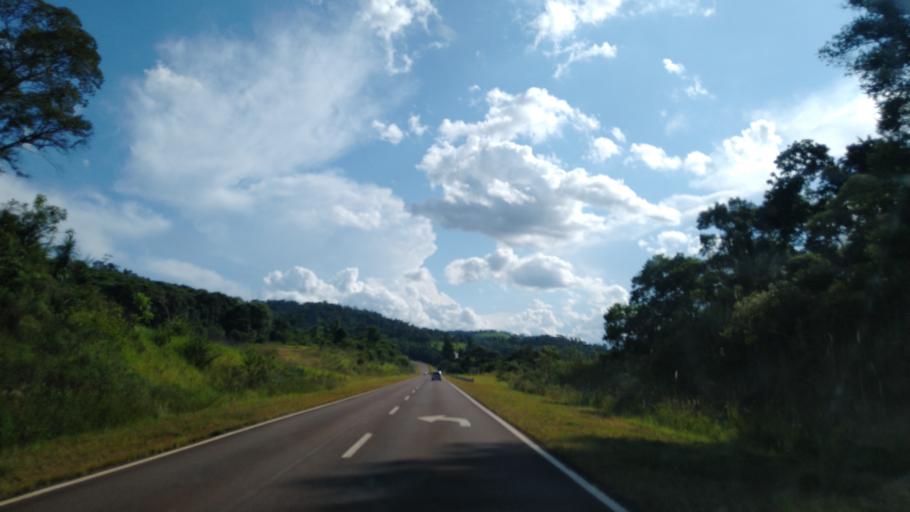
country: AR
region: Misiones
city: Bernardo de Irigoyen
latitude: -26.3320
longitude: -53.7633
